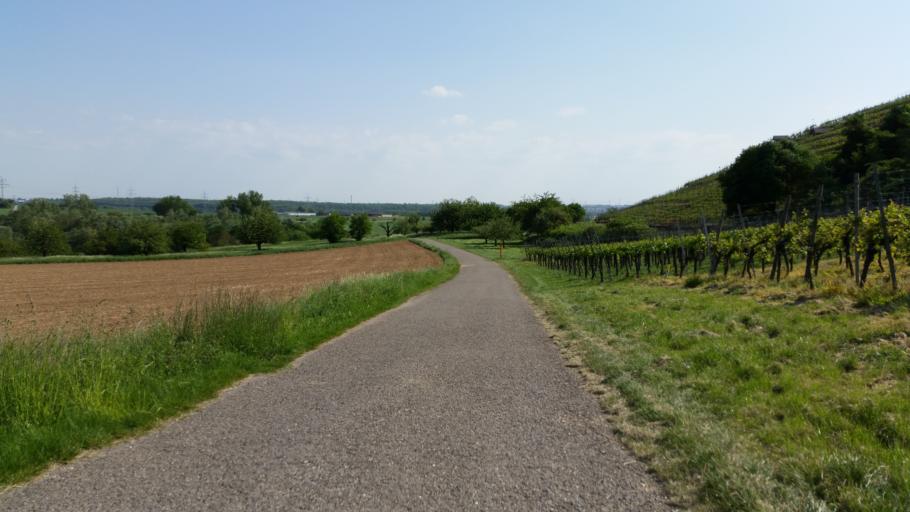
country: DE
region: Baden-Wuerttemberg
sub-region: Regierungsbezirk Stuttgart
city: Pleidelsheim
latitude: 48.9792
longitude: 9.2079
